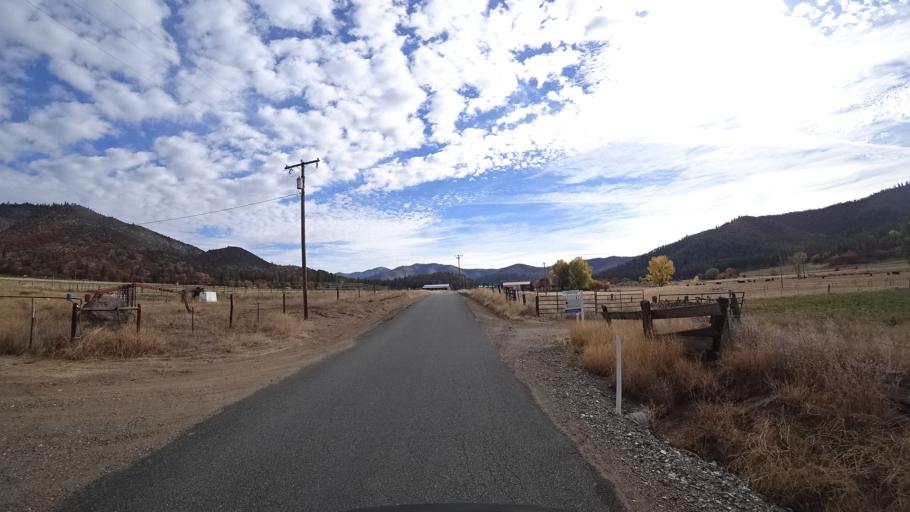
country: US
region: California
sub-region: Siskiyou County
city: Yreka
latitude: 41.6275
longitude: -122.8085
